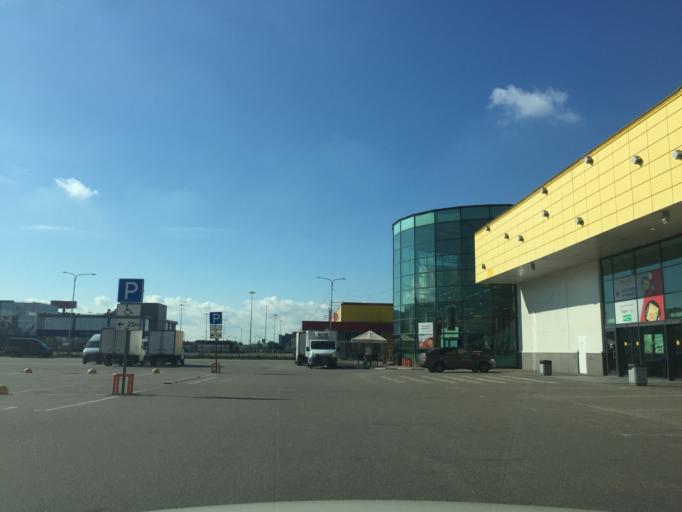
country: RU
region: St.-Petersburg
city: Kupchino
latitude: 59.8275
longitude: 30.3173
